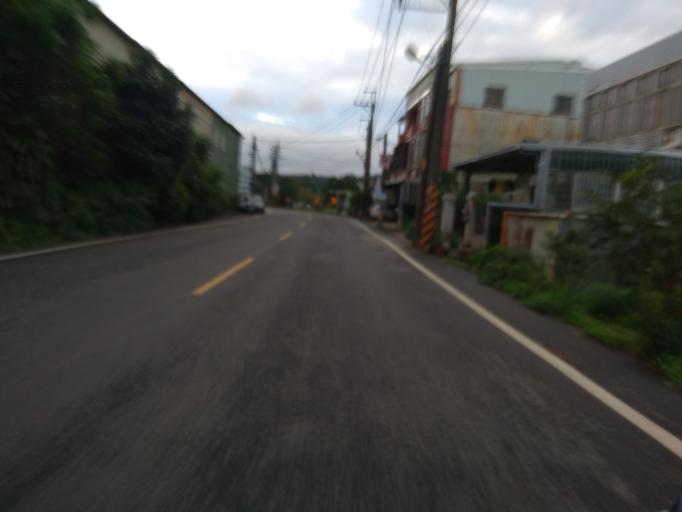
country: TW
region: Taiwan
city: Taoyuan City
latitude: 24.9461
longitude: 121.1883
